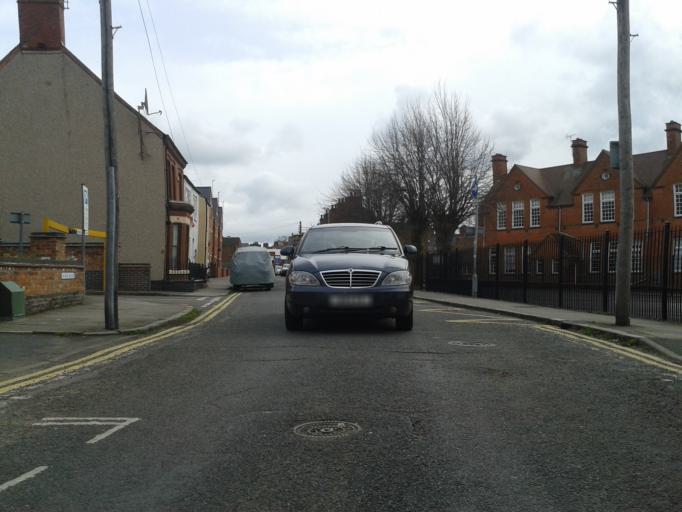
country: GB
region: England
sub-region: Leicestershire
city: Hinckley
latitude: 52.5449
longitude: -1.3703
